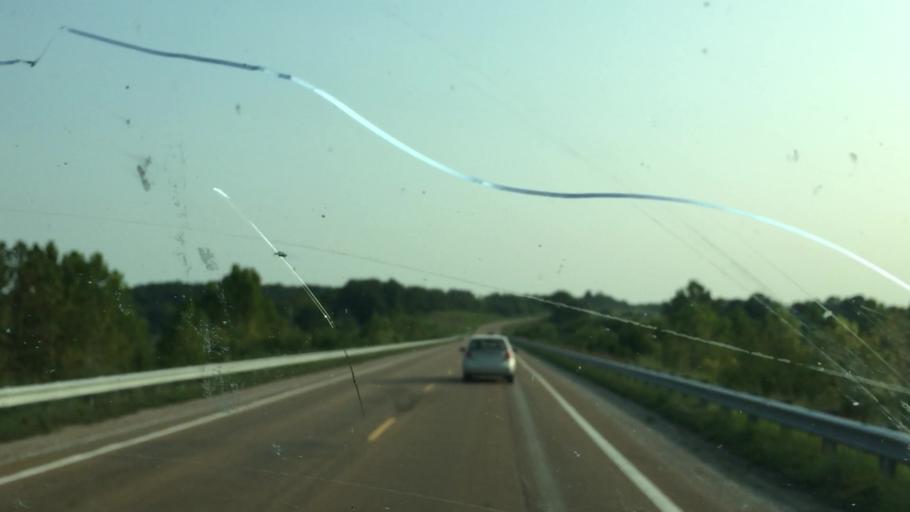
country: US
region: Missouri
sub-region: Pulaski County
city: Richland
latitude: 37.7963
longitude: -92.4063
